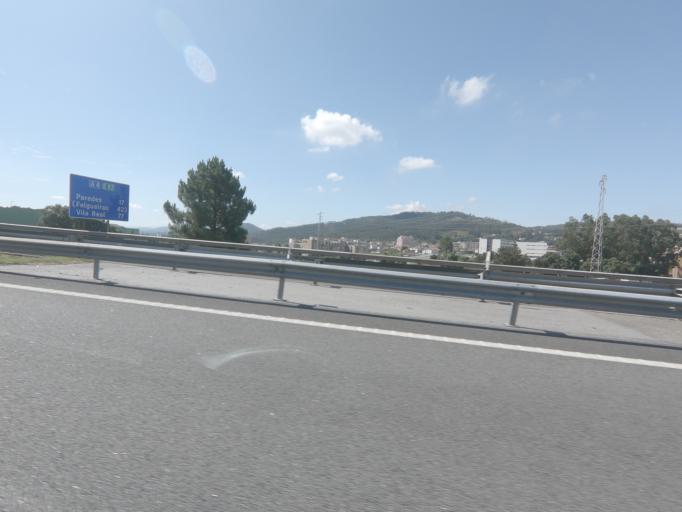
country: PT
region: Porto
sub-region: Valongo
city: Valongo
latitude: 41.1967
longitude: -8.4930
